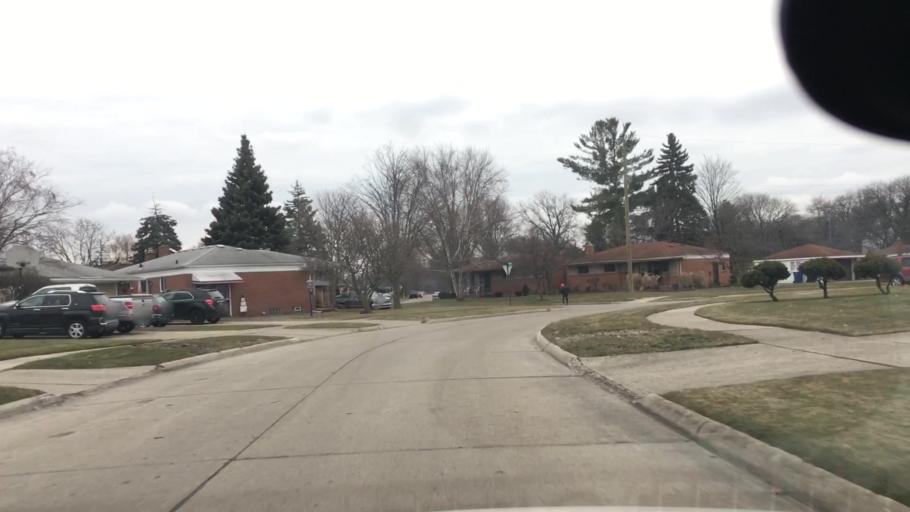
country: US
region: Michigan
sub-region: Oakland County
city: Madison Heights
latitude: 42.4958
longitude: -83.0712
